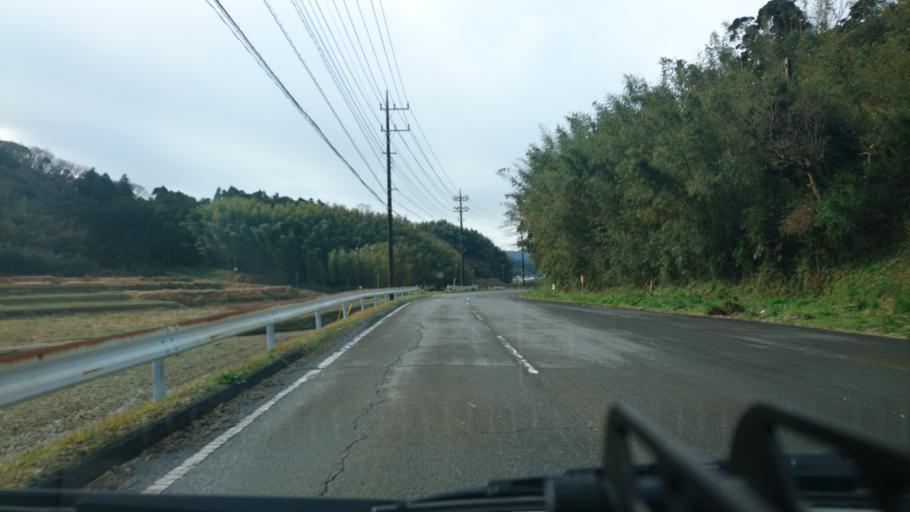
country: JP
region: Chiba
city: Kisarazu
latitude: 35.3164
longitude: 139.9640
